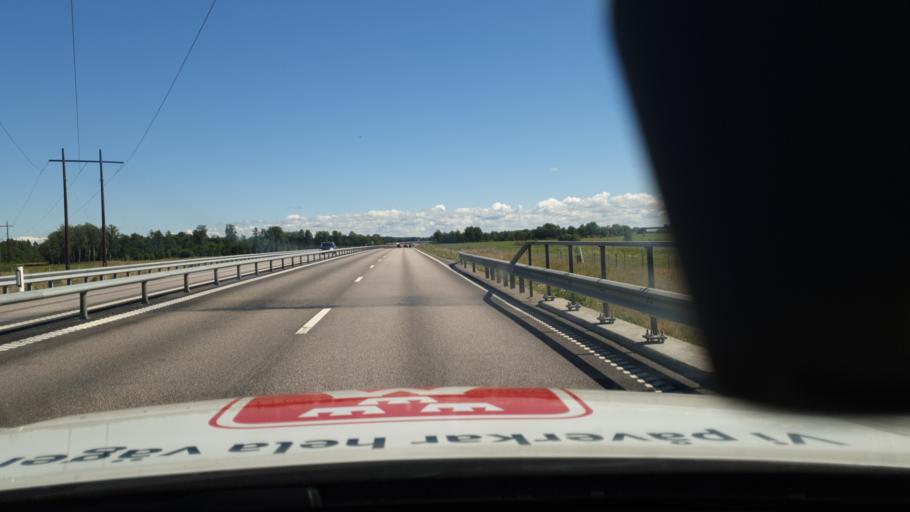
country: SE
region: Vaestra Goetaland
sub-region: Lidkopings Kommun
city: Vinninga
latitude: 58.4794
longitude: 13.2153
